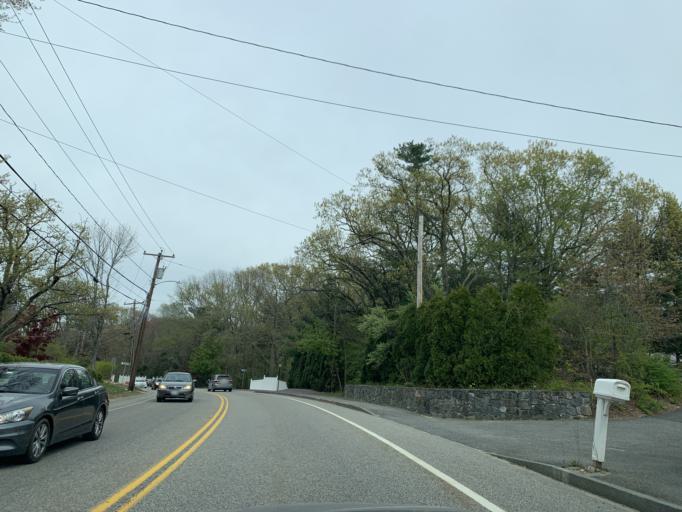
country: US
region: Massachusetts
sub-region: Norfolk County
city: Canton
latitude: 42.1365
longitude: -71.1563
